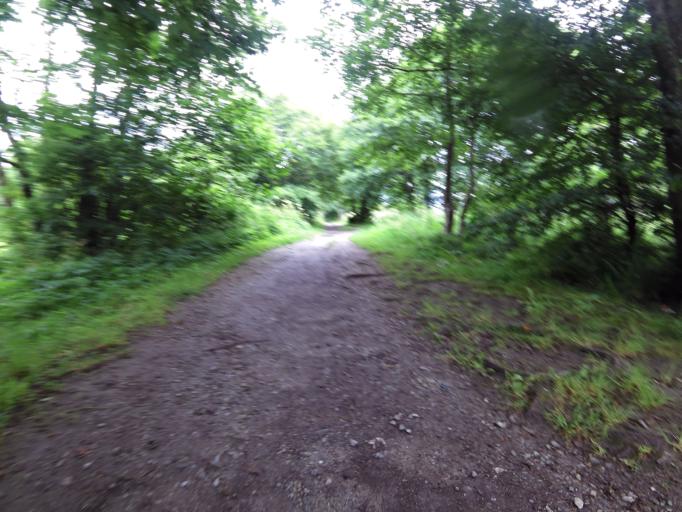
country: GB
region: Scotland
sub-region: Highland
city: Fort William
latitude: 56.8288
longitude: -5.0937
